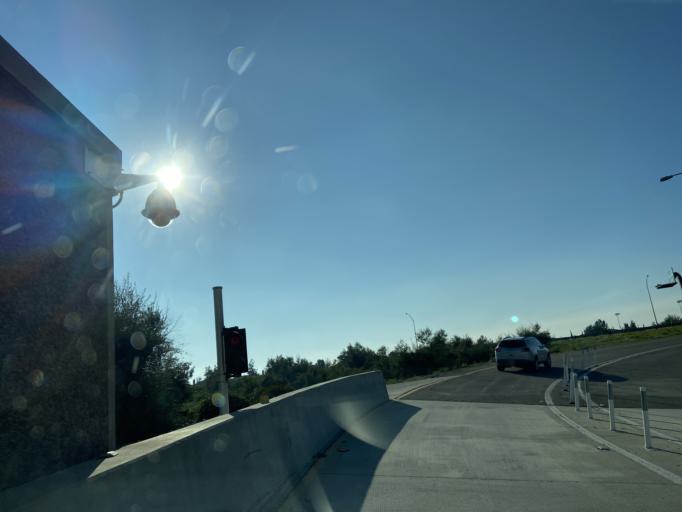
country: US
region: California
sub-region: San Diego County
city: Bonita
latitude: 32.6195
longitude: -116.9703
